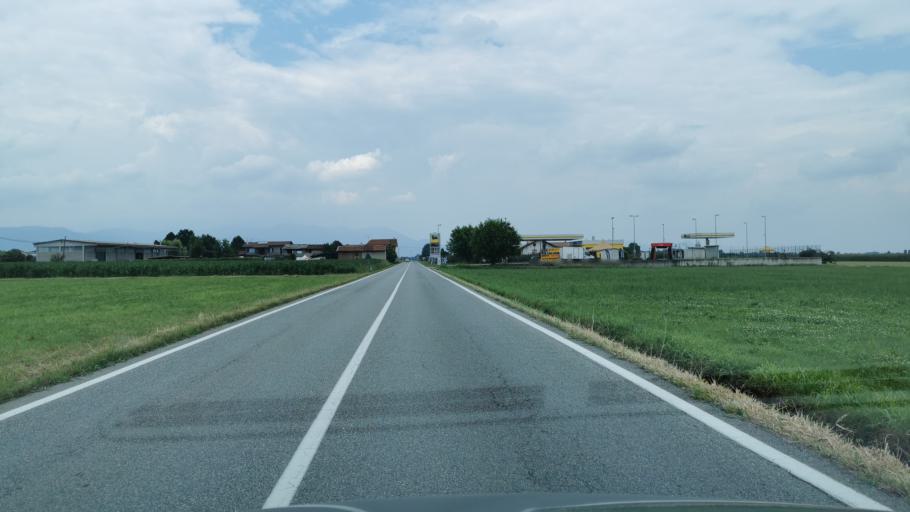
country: IT
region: Piedmont
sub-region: Provincia di Torino
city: Cavour
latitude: 44.8049
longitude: 7.3730
